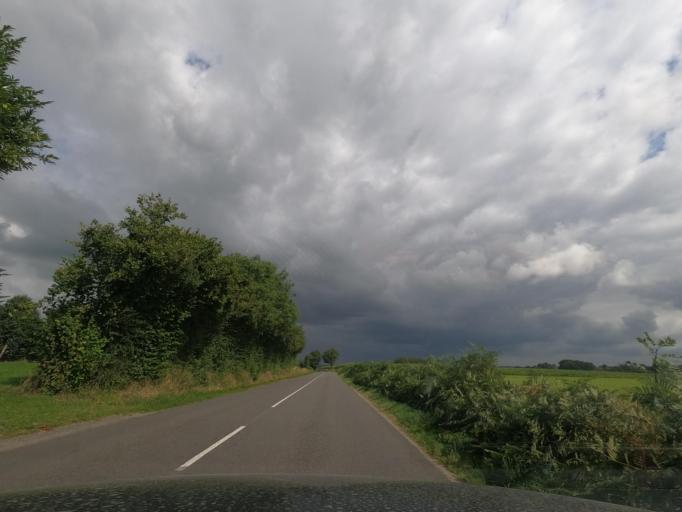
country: FR
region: Lower Normandy
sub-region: Departement de l'Orne
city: Briouze
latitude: 48.6917
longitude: -0.4317
